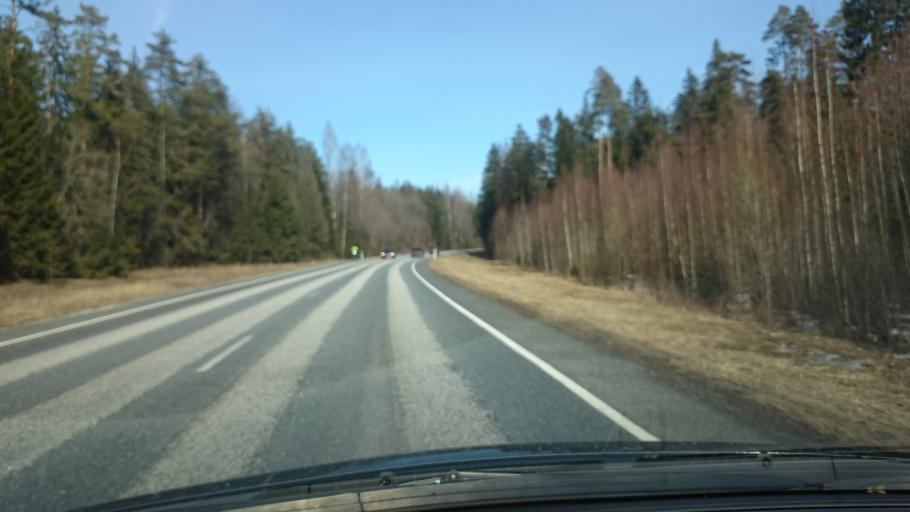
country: EE
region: Jaervamaa
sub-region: Tueri vald
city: Sarevere
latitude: 58.7399
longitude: 25.3020
